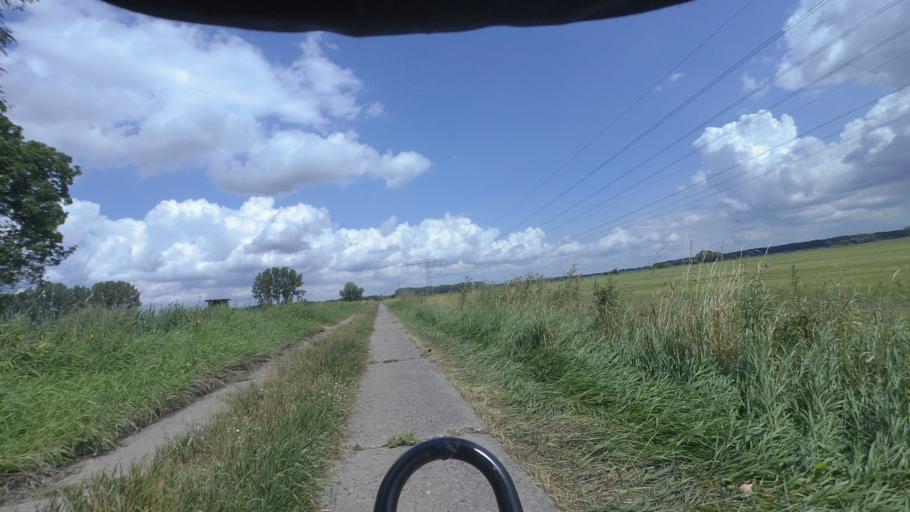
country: DE
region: Brandenburg
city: Grossbeeren
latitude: 52.3251
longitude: 13.3493
